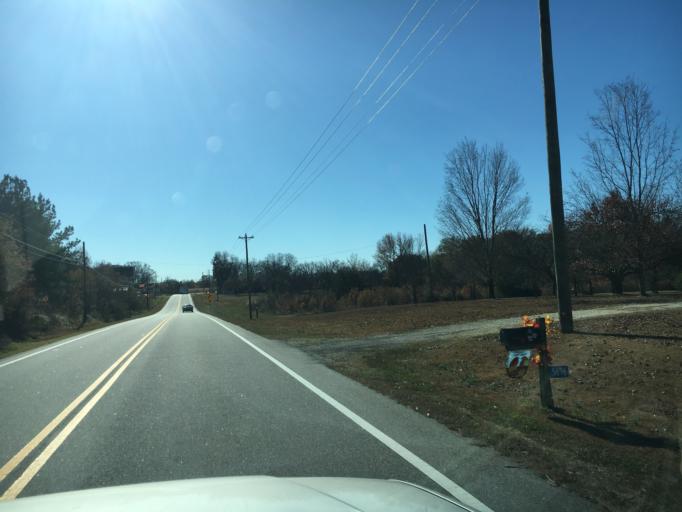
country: US
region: Georgia
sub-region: Hart County
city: Hartwell
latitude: 34.2989
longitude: -83.0050
